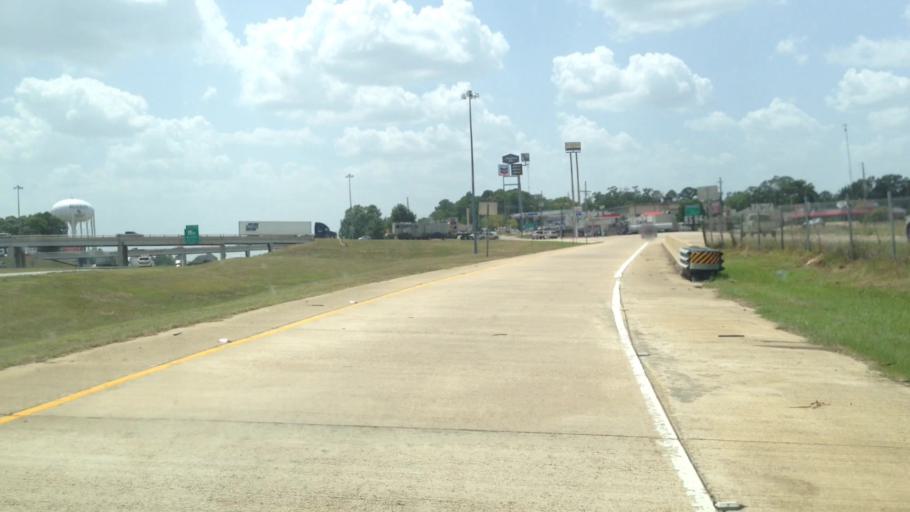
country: US
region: Louisiana
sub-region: Lincoln Parish
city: Ruston
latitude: 32.5405
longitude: -92.6355
